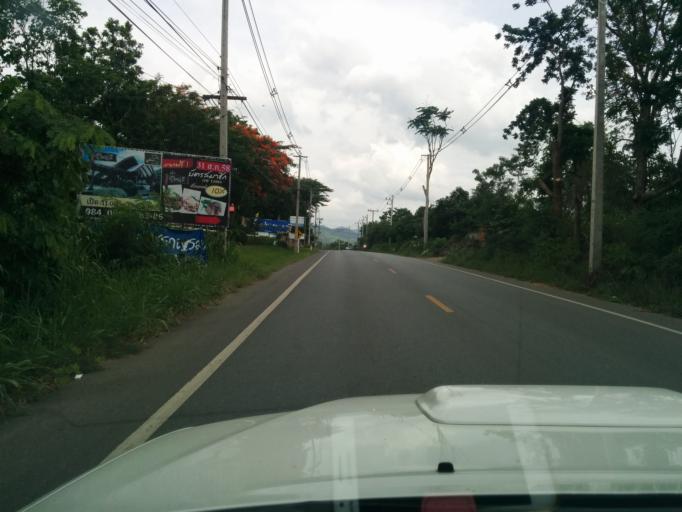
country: TH
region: Sara Buri
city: Muak Lek
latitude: 14.6115
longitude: 101.2123
